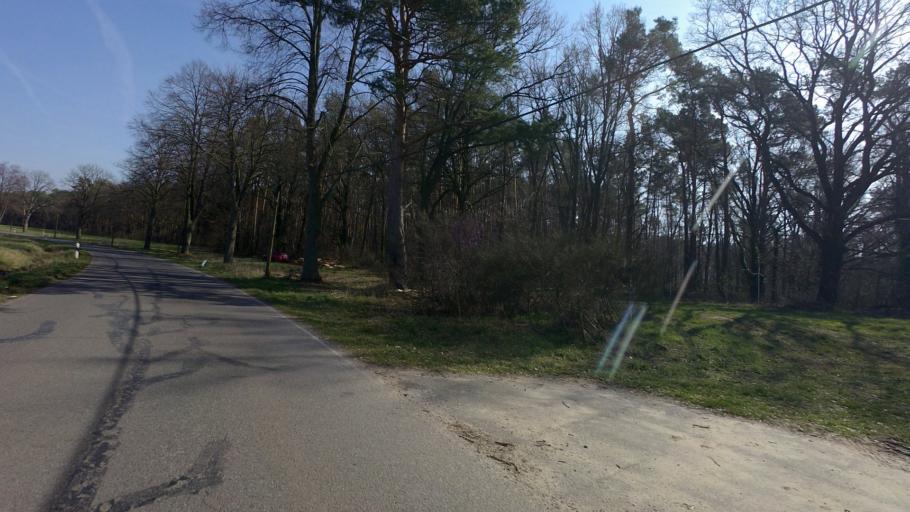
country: DE
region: Brandenburg
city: Golssen
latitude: 51.9825
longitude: 13.5482
